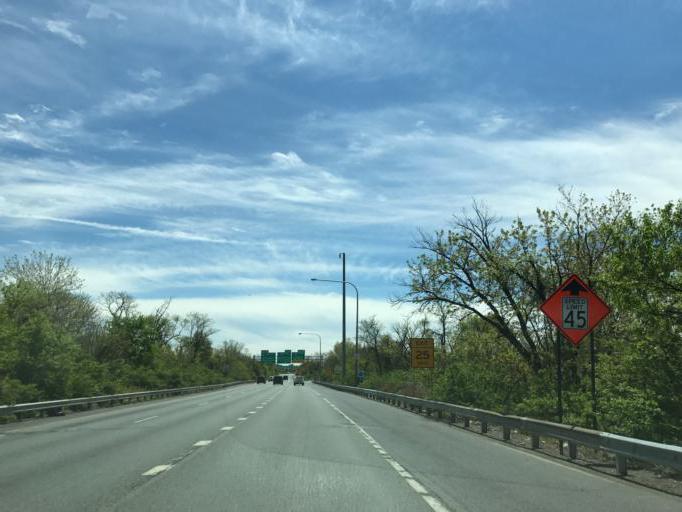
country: US
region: Delaware
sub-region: New Castle County
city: Newport
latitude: 39.7071
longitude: -75.6074
